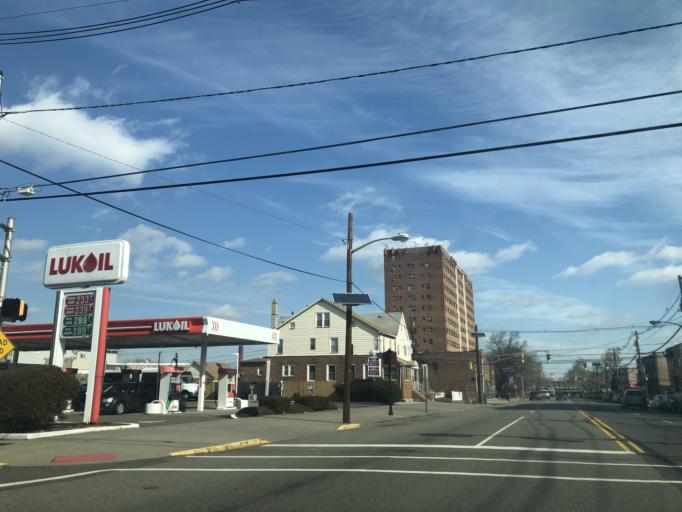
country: US
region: New Jersey
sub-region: Hudson County
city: Bayonne
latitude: 40.6877
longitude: -74.1071
